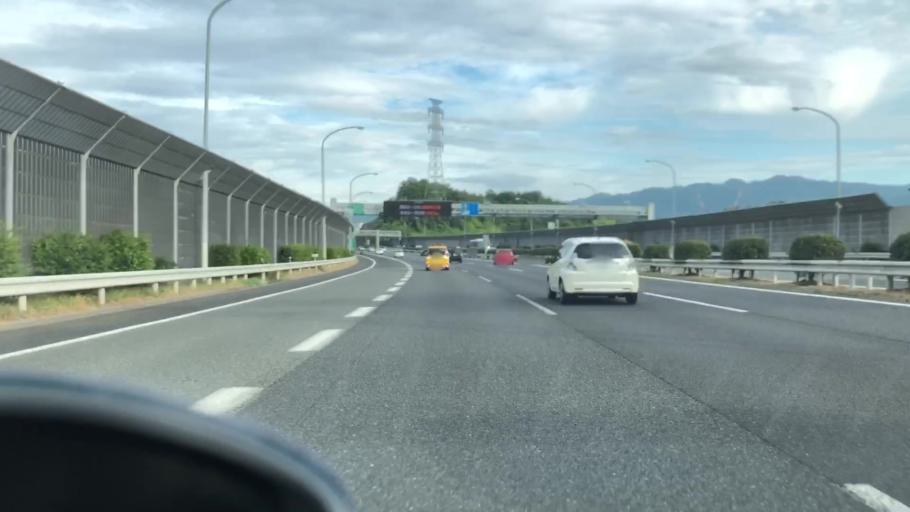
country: JP
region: Hyogo
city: Sandacho
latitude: 34.8414
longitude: 135.2288
